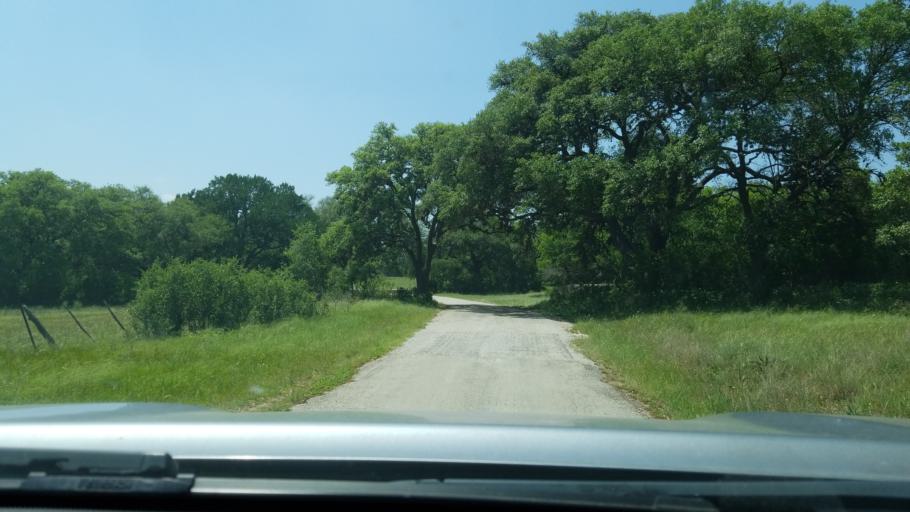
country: US
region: Texas
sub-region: Blanco County
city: Blanco
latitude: 30.0154
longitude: -98.4486
